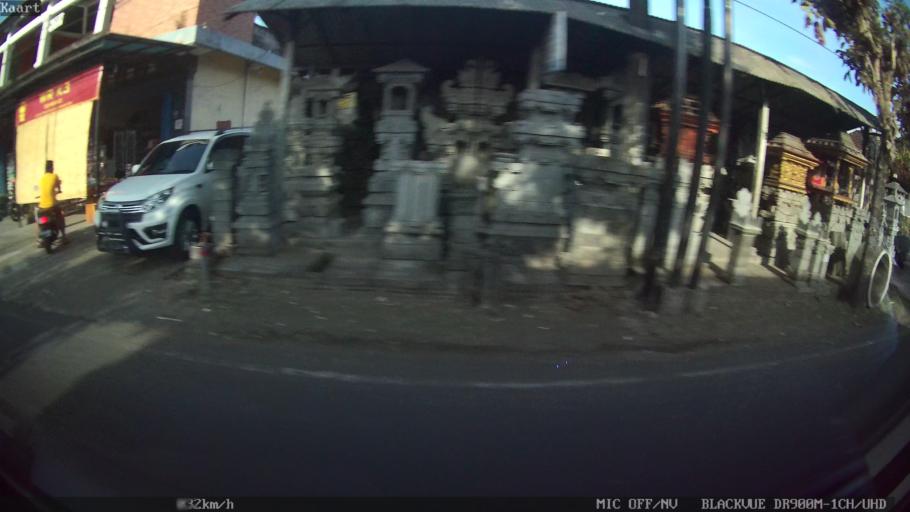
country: ID
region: Bali
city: Banjar Batur
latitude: -8.6091
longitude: 115.2134
